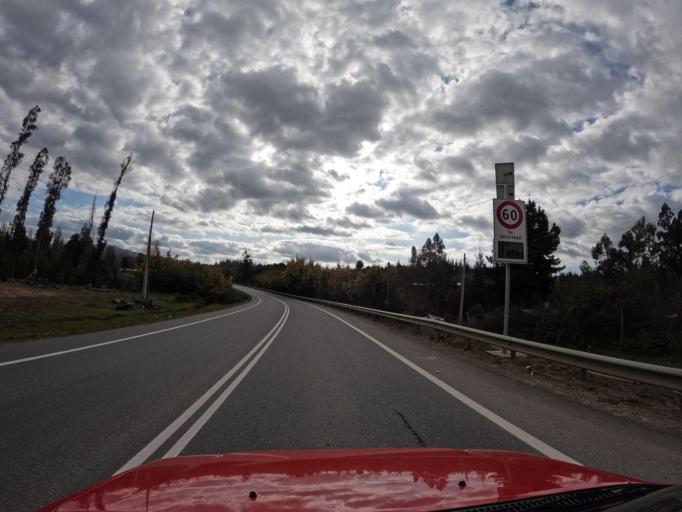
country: CL
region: Maule
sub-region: Provincia de Linares
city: San Javier
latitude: -35.5585
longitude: -72.0827
